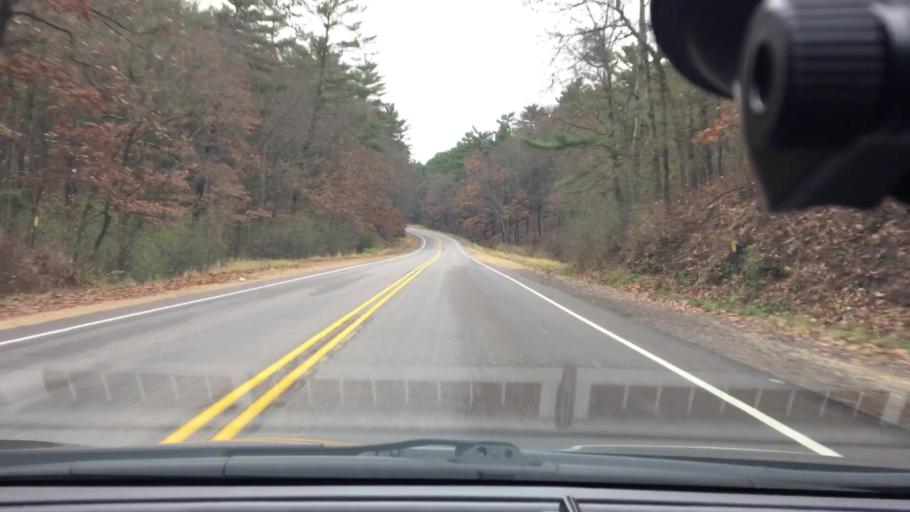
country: US
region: Wisconsin
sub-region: Columbia County
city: Wisconsin Dells
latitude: 43.6459
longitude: -89.8064
